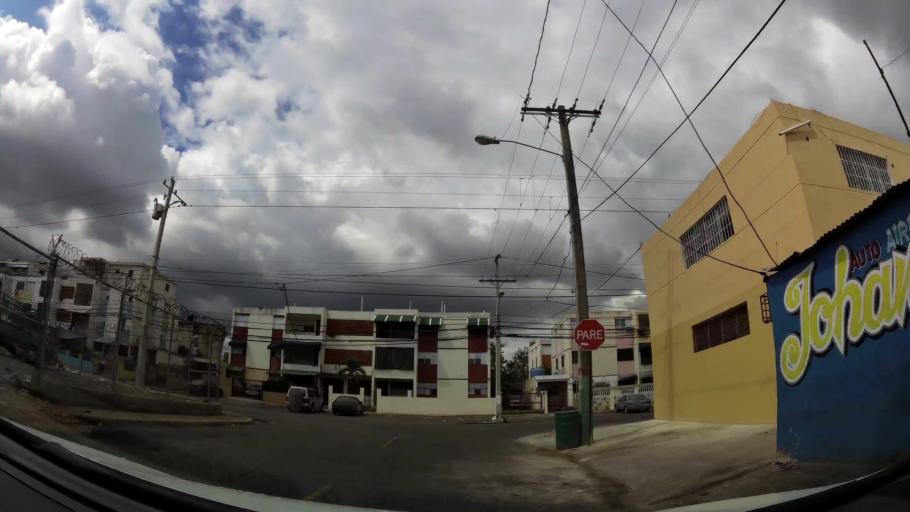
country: DO
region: Nacional
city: La Agustina
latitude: 18.4932
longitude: -69.9276
